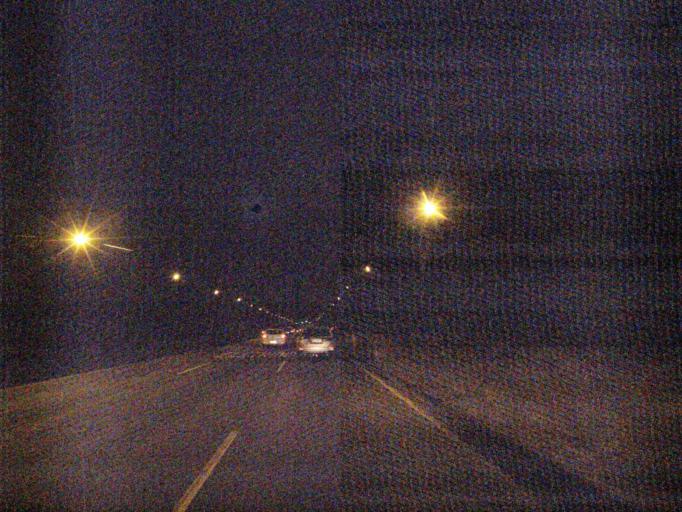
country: BR
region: Rio de Janeiro
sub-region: Rio De Janeiro
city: Rio de Janeiro
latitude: -22.9525
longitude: -43.2049
